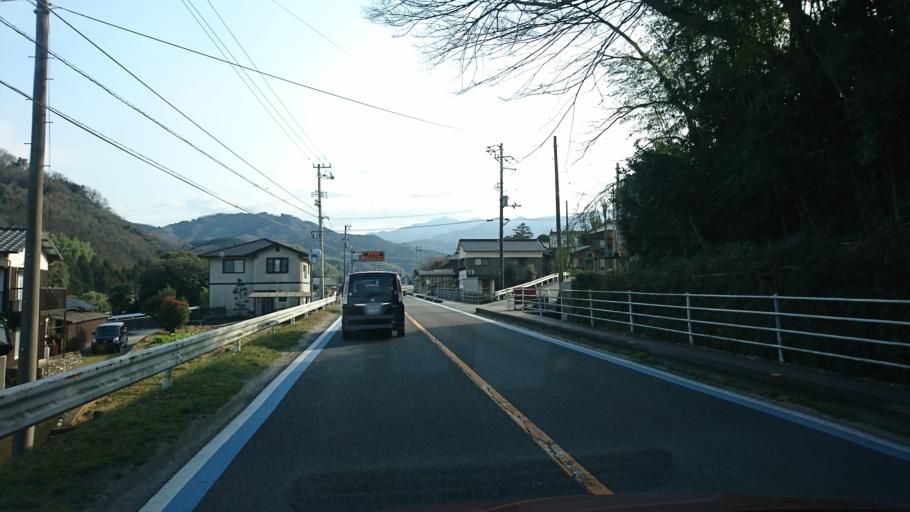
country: JP
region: Ehime
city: Hojo
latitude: 34.0082
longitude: 132.9380
